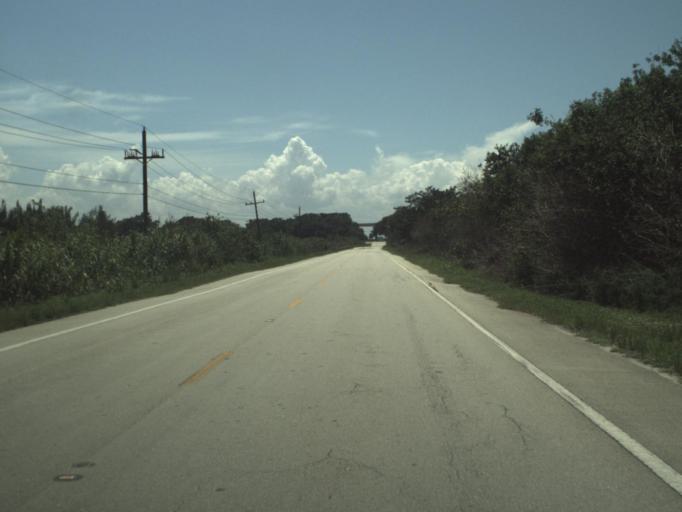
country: US
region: Florida
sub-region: Martin County
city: Indiantown
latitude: 26.9861
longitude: -80.6087
